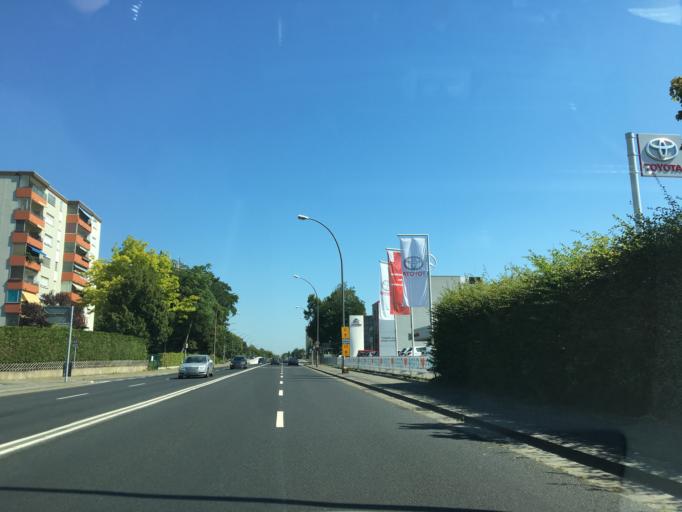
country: DE
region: Hesse
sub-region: Regierungsbezirk Darmstadt
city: Russelsheim
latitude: 49.9791
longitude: 8.4280
